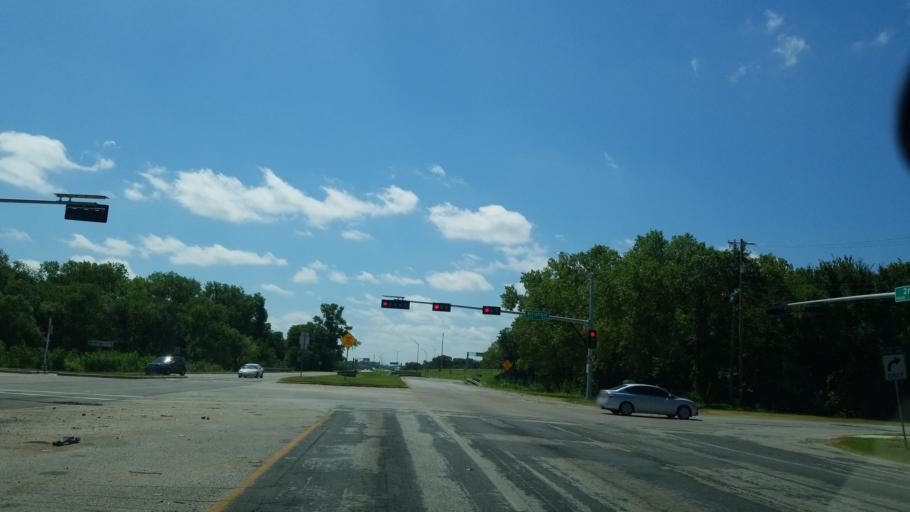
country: US
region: Texas
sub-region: Dallas County
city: Dallas
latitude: 32.7478
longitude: -96.7291
